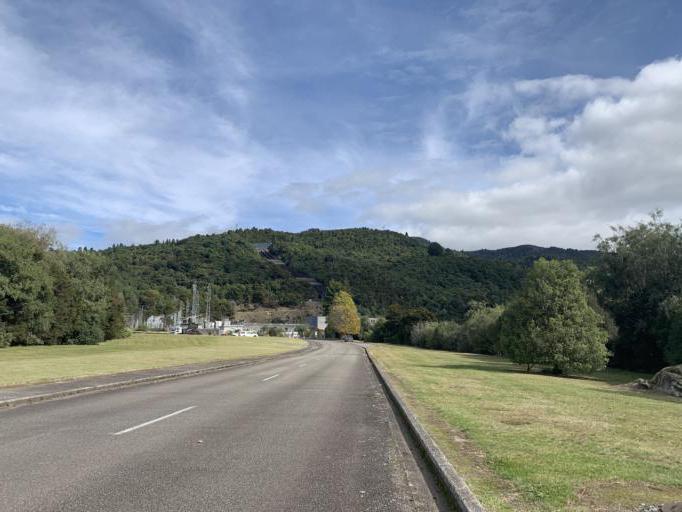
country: NZ
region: Waikato
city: Turangi
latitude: -38.9805
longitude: 175.7723
